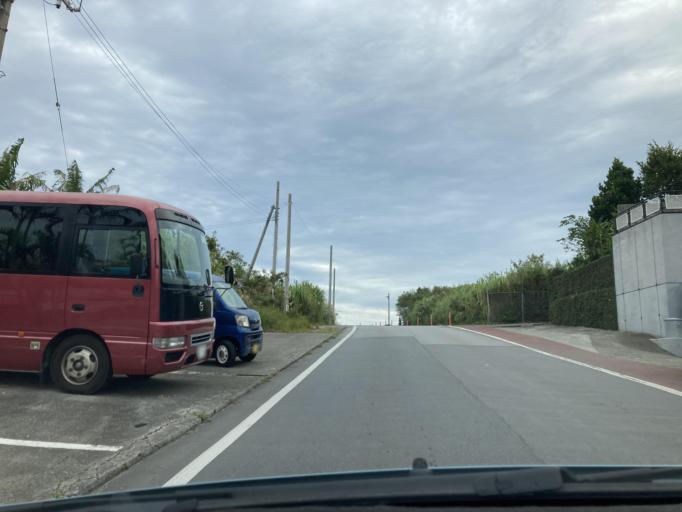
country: JP
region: Okinawa
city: Okinawa
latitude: 26.3861
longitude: 127.7398
